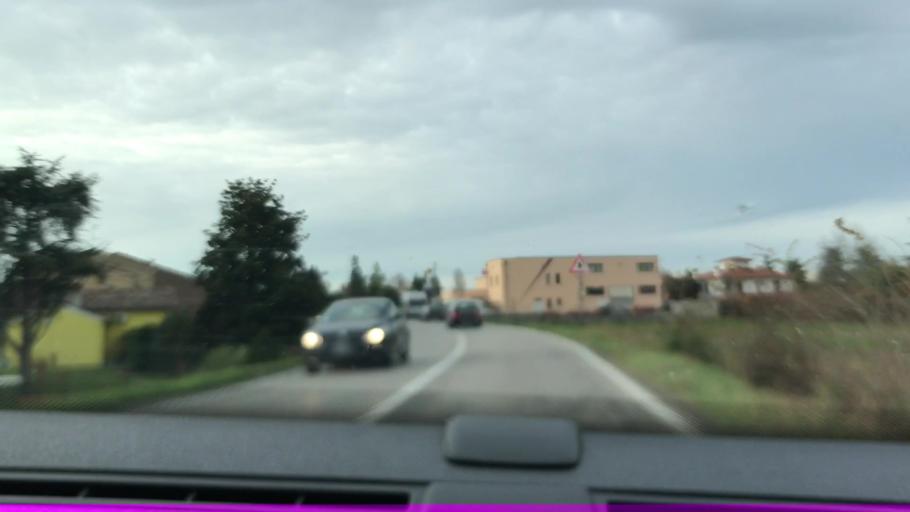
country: IT
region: Lombardy
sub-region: Provincia di Mantova
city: San Benedetto Po
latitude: 45.0345
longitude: 10.9335
